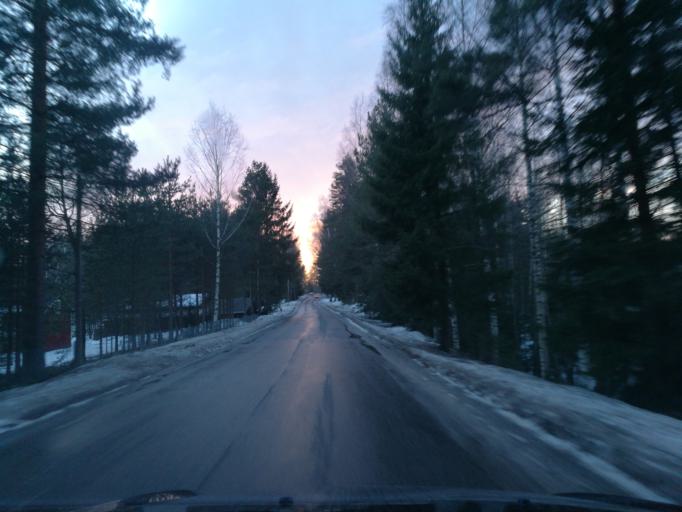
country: FI
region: Uusimaa
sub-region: Helsinki
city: Kerava
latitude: 60.3981
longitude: 25.1720
